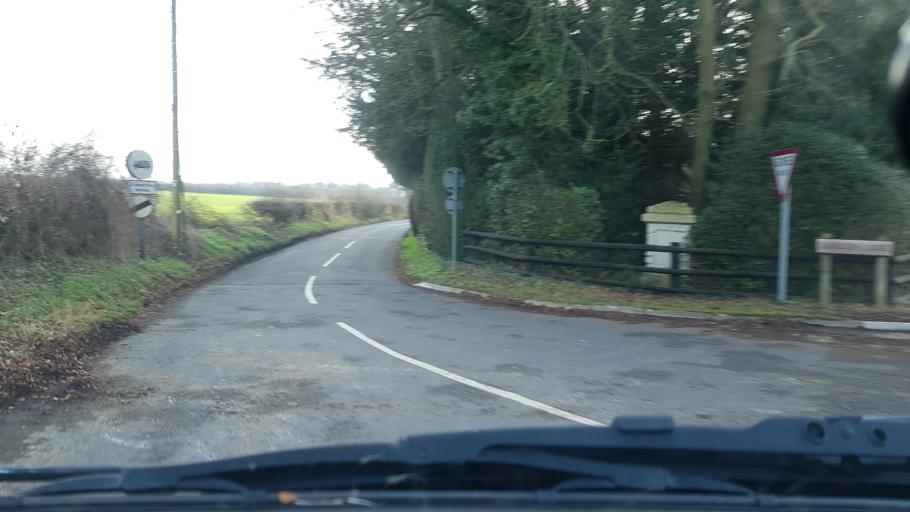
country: GB
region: England
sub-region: Hampshire
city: Abbotts Ann
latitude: 51.2170
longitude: -1.5588
